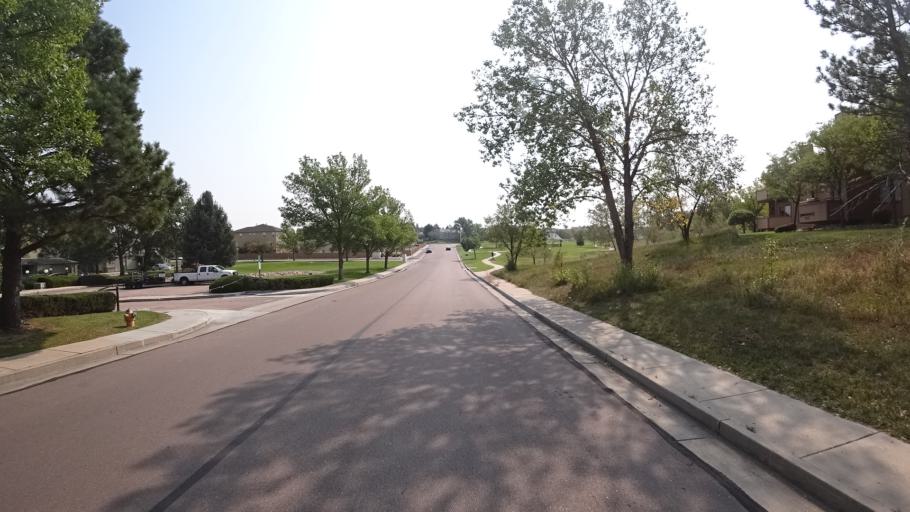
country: US
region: Colorado
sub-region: El Paso County
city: Stratmoor
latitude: 38.8189
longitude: -104.7643
